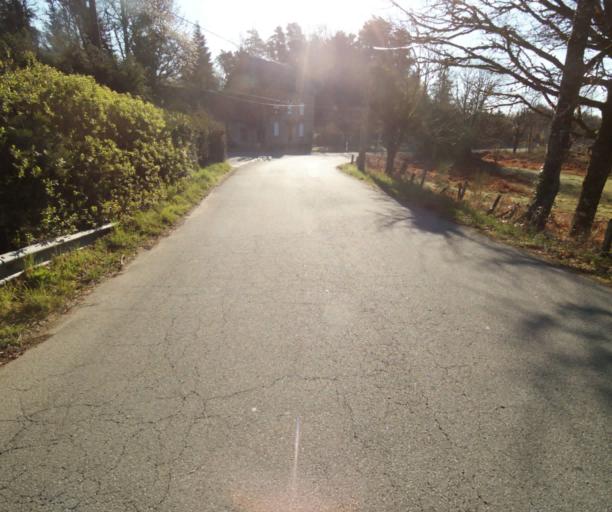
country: FR
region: Limousin
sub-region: Departement de la Correze
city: Correze
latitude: 45.3227
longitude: 1.8776
